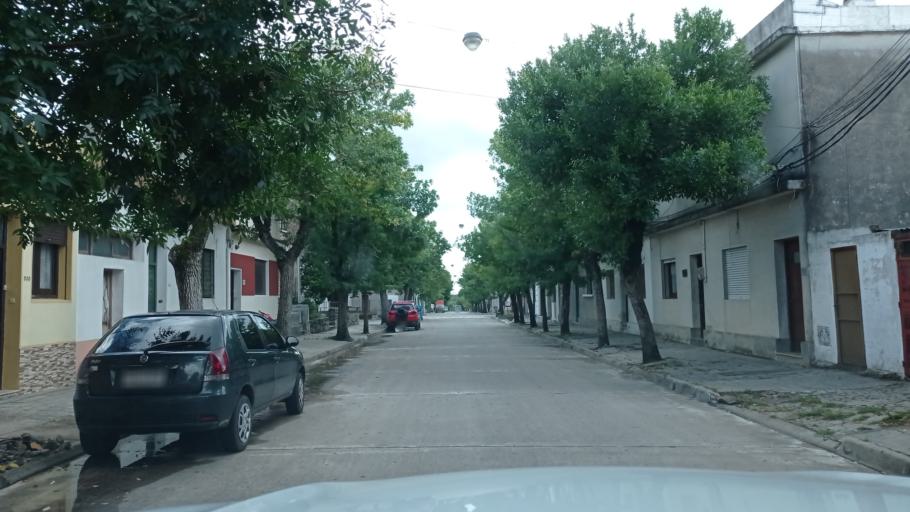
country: UY
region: Florida
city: Florida
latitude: -34.0944
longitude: -56.2169
